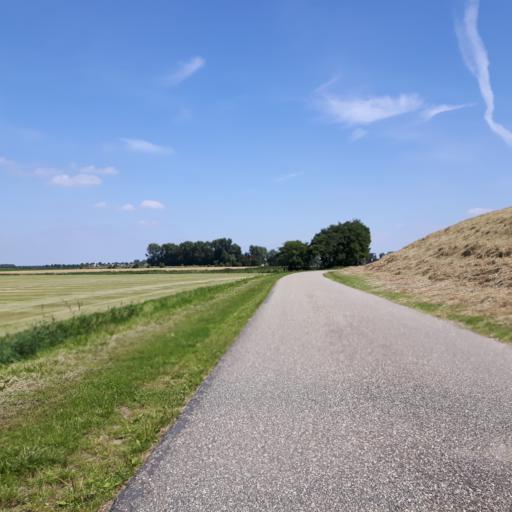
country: NL
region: Zeeland
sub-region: Schouwen-Duiveland
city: Bruinisse
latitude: 51.6138
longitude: 4.1414
